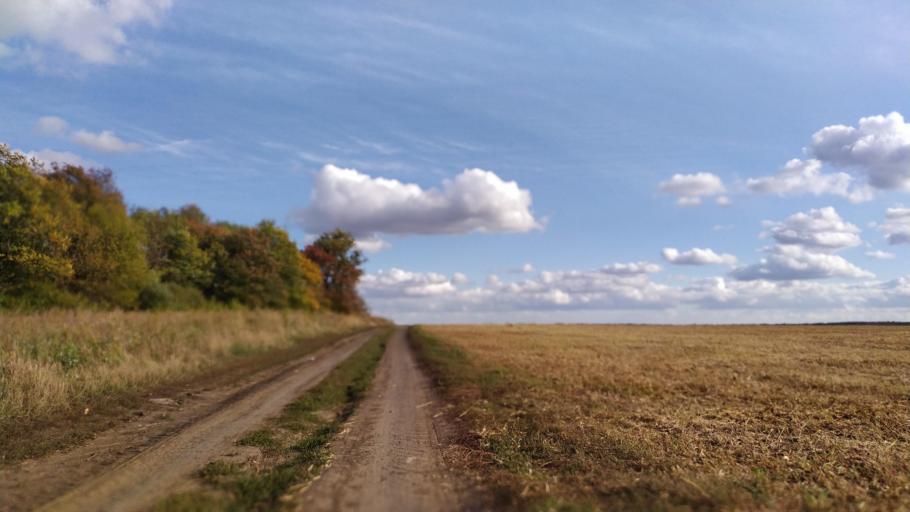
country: RU
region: Kursk
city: Kursk
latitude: 51.6131
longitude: 36.1645
